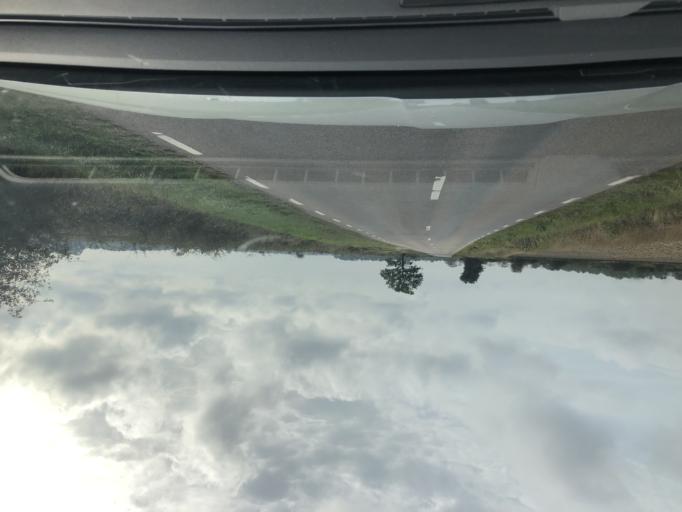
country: SE
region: Kalmar
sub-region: Morbylanga Kommun
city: Moerbylanga
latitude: 56.3116
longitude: 16.4068
